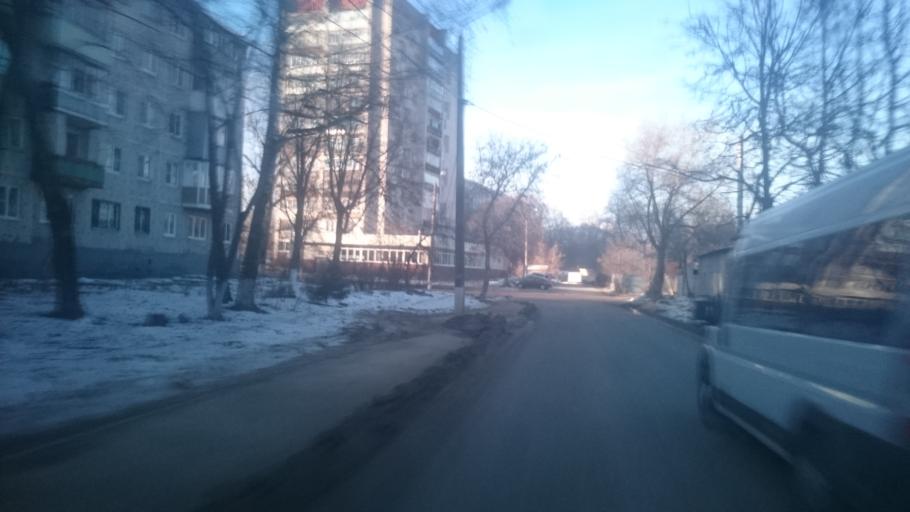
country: RU
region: Tula
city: Tula
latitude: 54.1810
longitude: 37.6390
